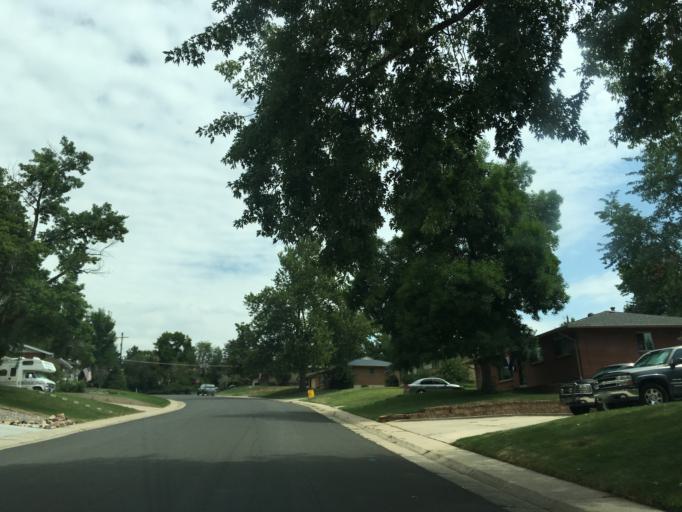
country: US
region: Colorado
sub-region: Arapahoe County
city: Sheridan
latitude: 39.6664
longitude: -105.0510
